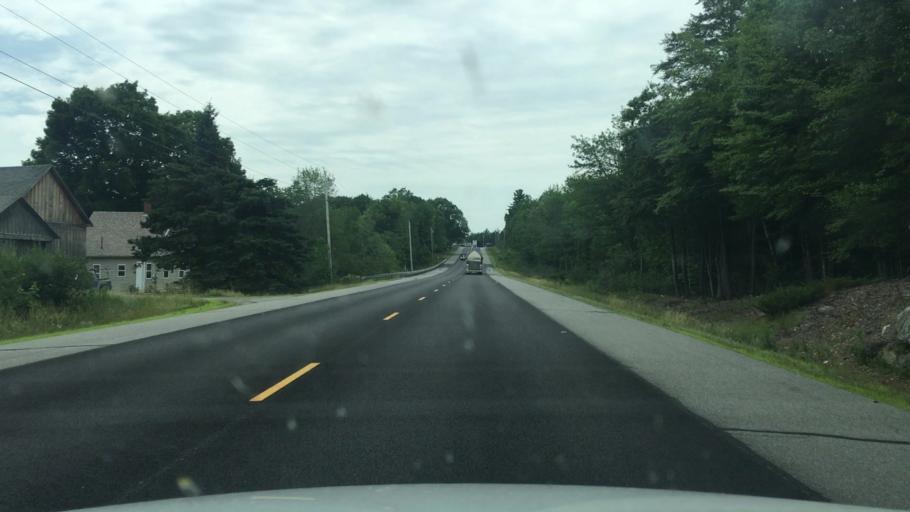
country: US
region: Maine
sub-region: Knox County
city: Washington
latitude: 44.3906
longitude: -69.3551
